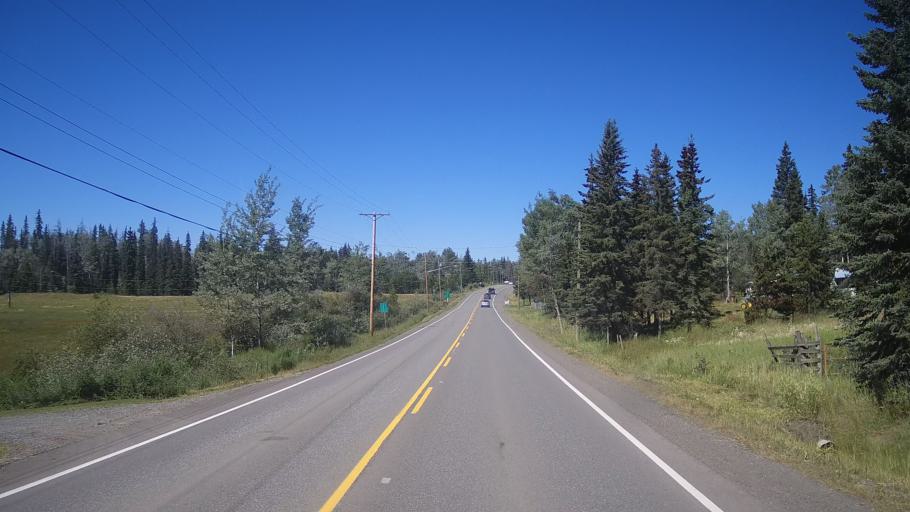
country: CA
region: British Columbia
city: Cache Creek
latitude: 51.5547
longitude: -121.2116
